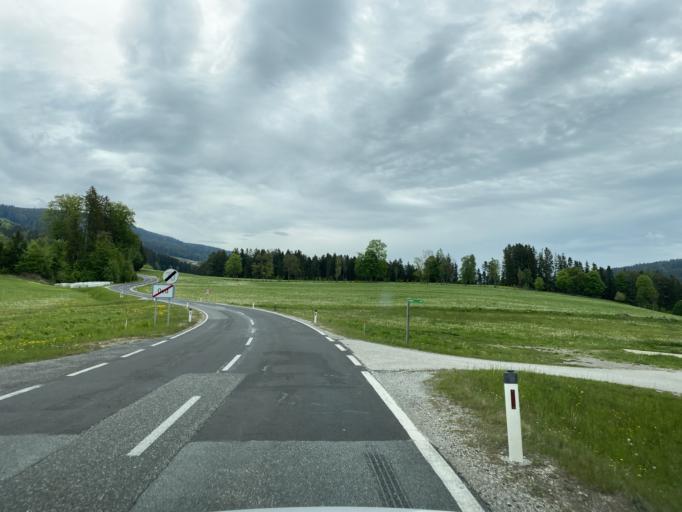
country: AT
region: Styria
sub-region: Politischer Bezirk Weiz
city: Gschaid bei Birkfeld
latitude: 47.3459
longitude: 15.7149
